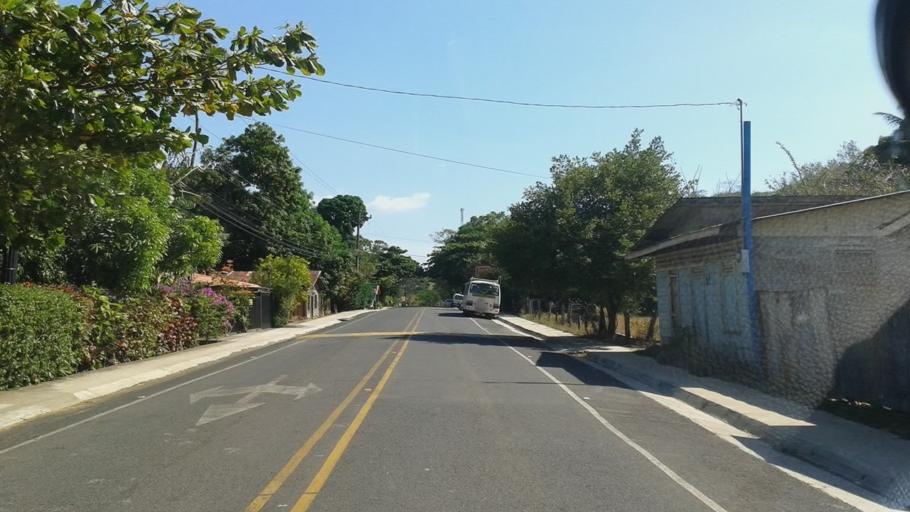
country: CR
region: Guanacaste
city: Santa Cruz
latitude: 10.2112
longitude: -85.7584
